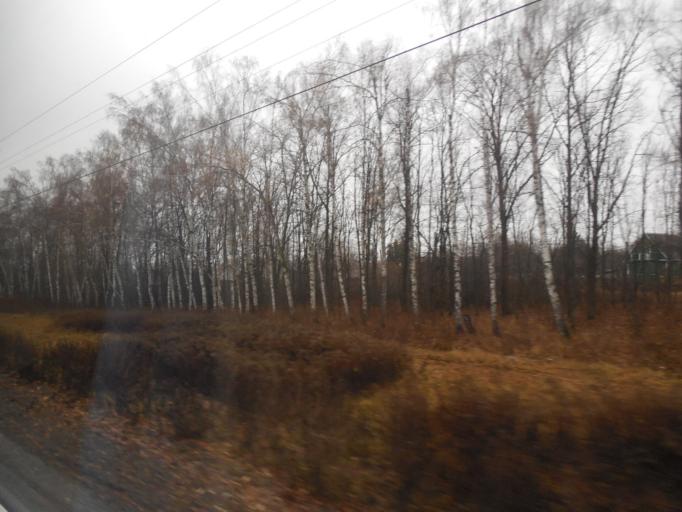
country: RU
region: Moskovskaya
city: Vostryakovo
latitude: 55.4001
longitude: 37.8015
